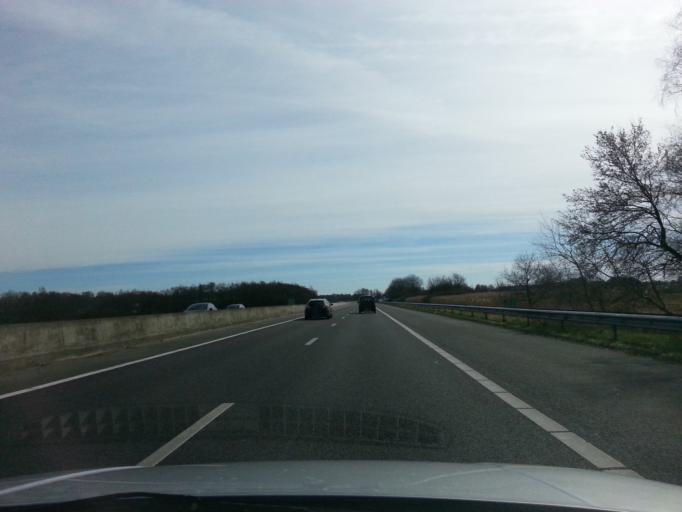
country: NL
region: Groningen
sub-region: Gemeente Haren
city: Haren
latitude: 53.1540
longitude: 6.6003
